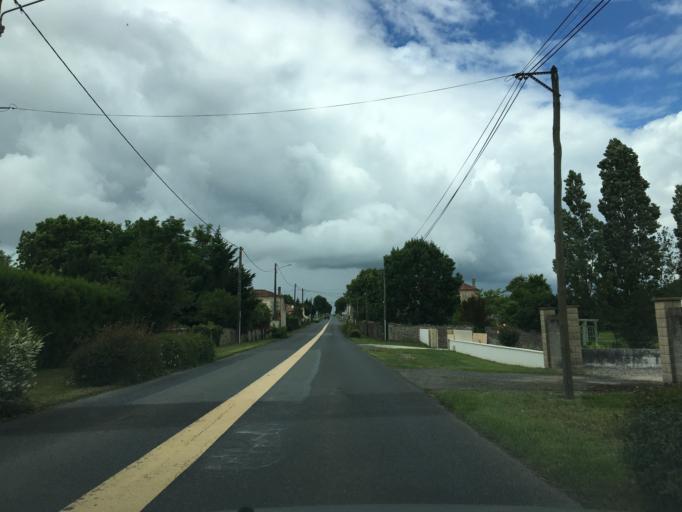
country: FR
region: Poitou-Charentes
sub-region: Departement des Deux-Sevres
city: Beauvoir-sur-Niort
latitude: 46.0749
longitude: -0.5065
